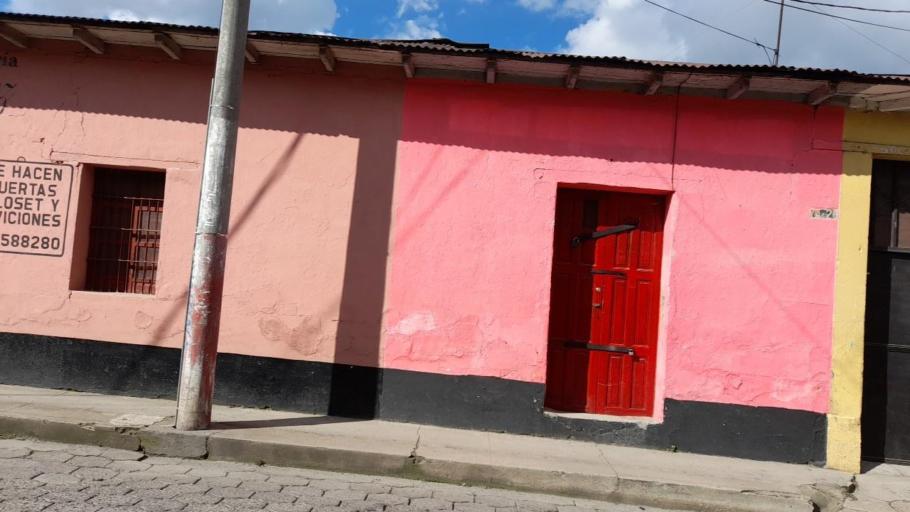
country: GT
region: Quetzaltenango
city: Quetzaltenango
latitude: 14.8311
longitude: -91.5171
